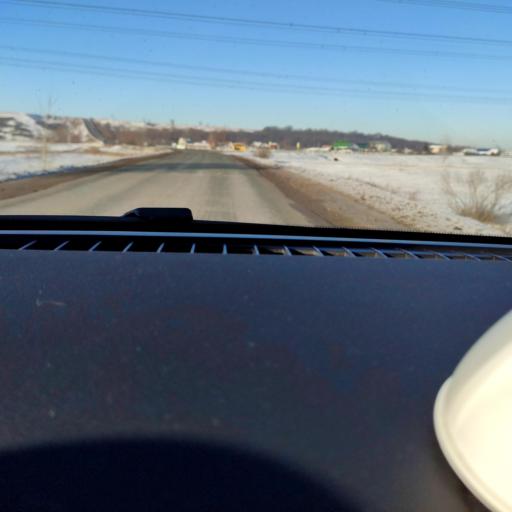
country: RU
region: Samara
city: Spiridonovka
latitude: 53.1417
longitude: 50.5963
